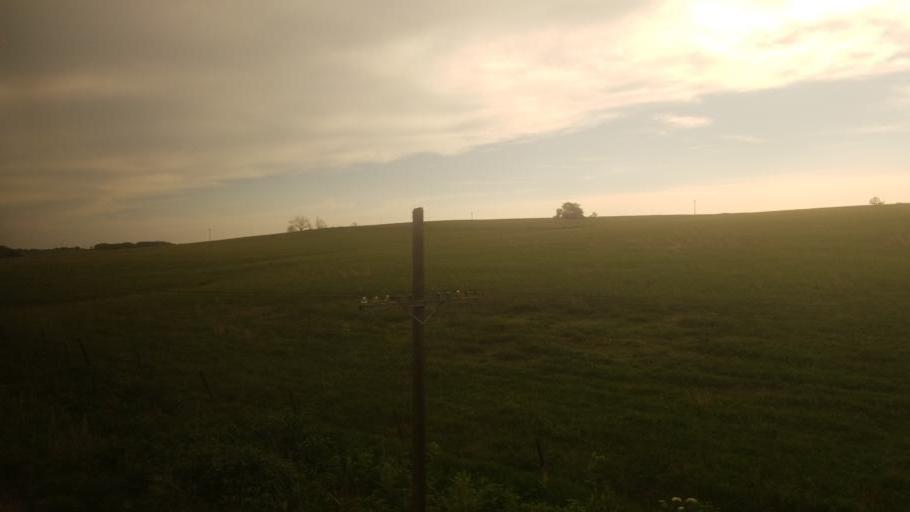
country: US
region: Kansas
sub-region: Osage County
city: Carbondale
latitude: 38.9000
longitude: -95.7000
